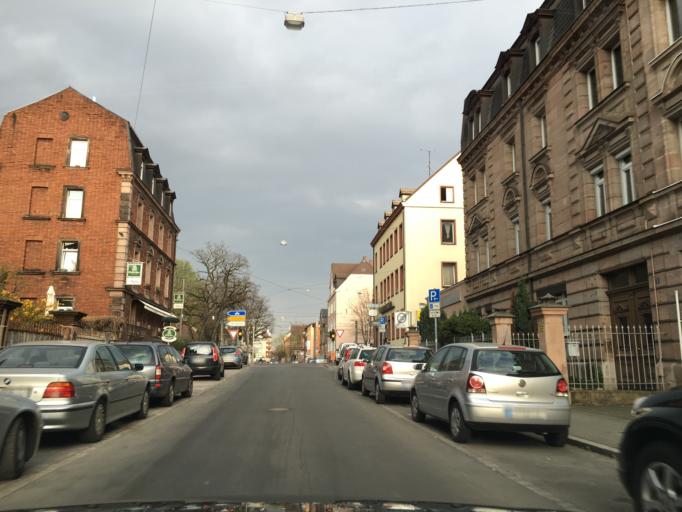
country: DE
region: Bavaria
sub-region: Regierungsbezirk Mittelfranken
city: Nuernberg
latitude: 49.4609
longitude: 11.0714
